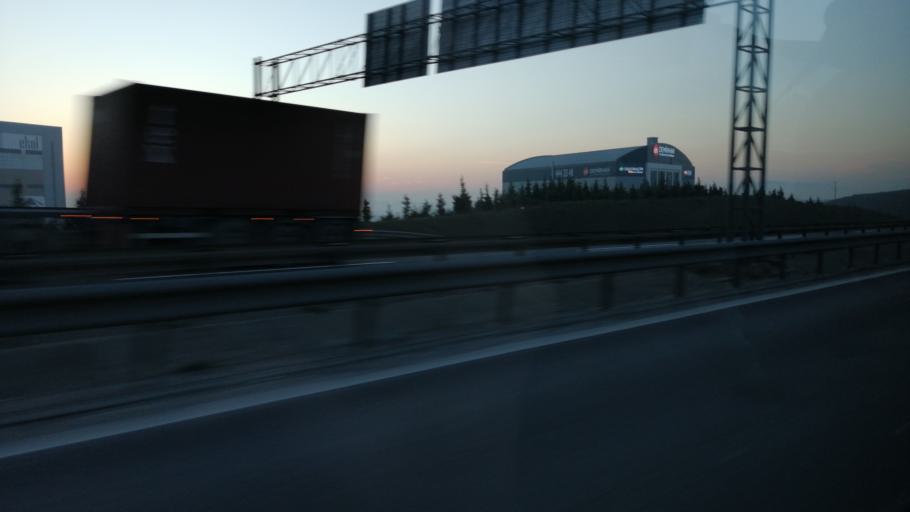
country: TR
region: Kocaeli
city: Balcik
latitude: 40.8573
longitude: 29.4065
